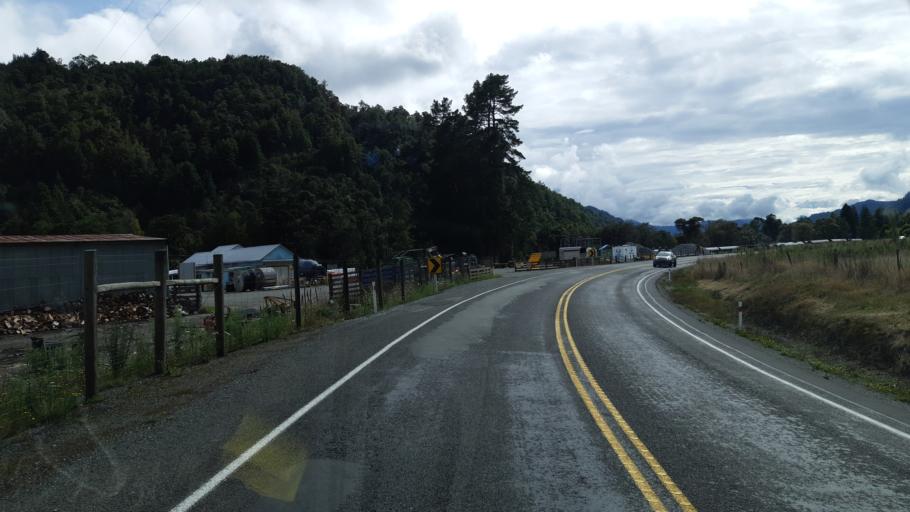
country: NZ
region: West Coast
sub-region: Buller District
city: Westport
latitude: -41.7920
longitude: 172.3655
